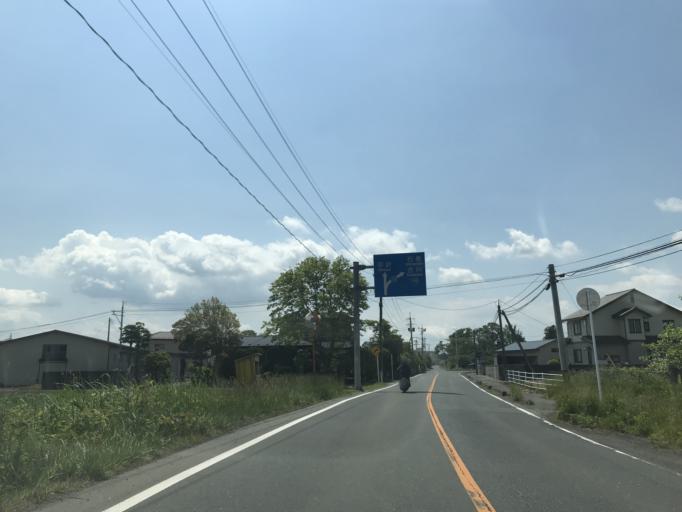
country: JP
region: Miyagi
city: Kogota
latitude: 38.5664
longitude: 141.0461
